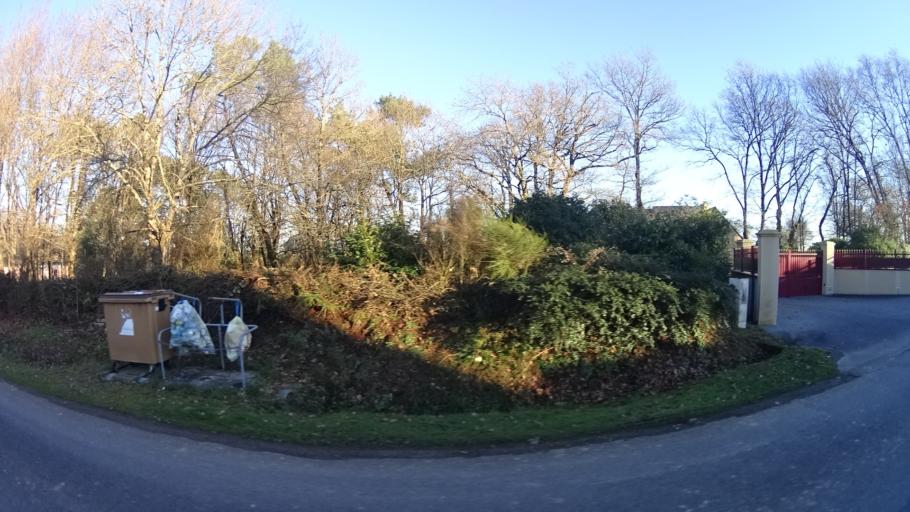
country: FR
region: Brittany
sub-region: Departement du Morbihan
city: Saint-Jean-la-Poterie
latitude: 47.6398
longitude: -2.1314
